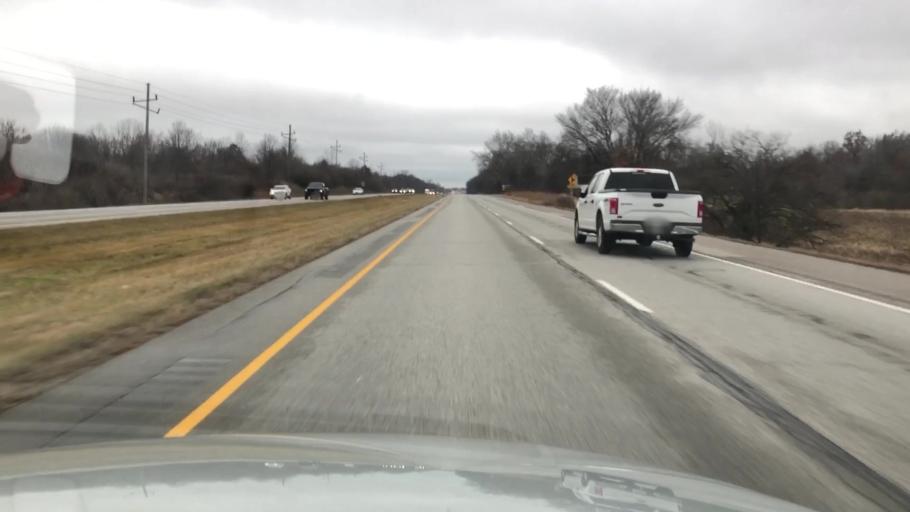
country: US
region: Indiana
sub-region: Kosciusko County
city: Pierceton
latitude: 41.2132
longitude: -85.7503
